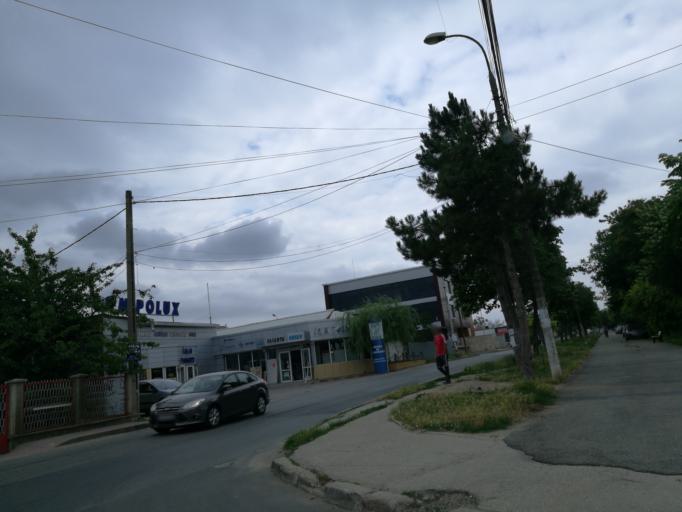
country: RO
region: Constanta
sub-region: Municipiul Mangalia
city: Mangalia
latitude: 43.8139
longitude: 28.5723
